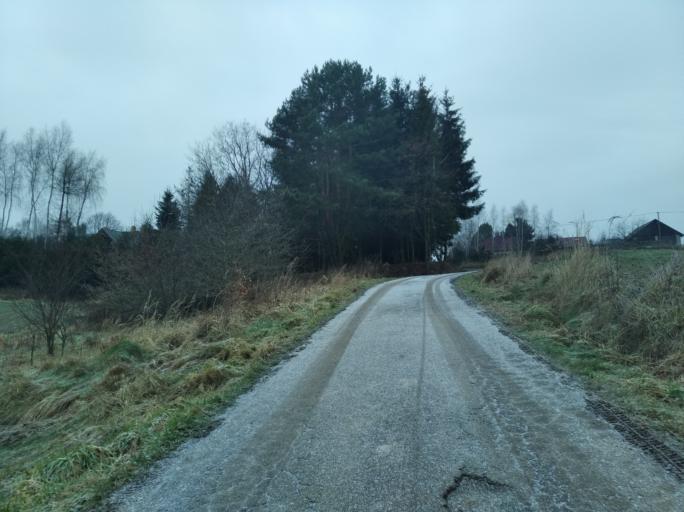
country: PL
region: Subcarpathian Voivodeship
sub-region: Powiat strzyzowski
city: Strzyzow
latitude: 49.8498
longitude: 21.7830
